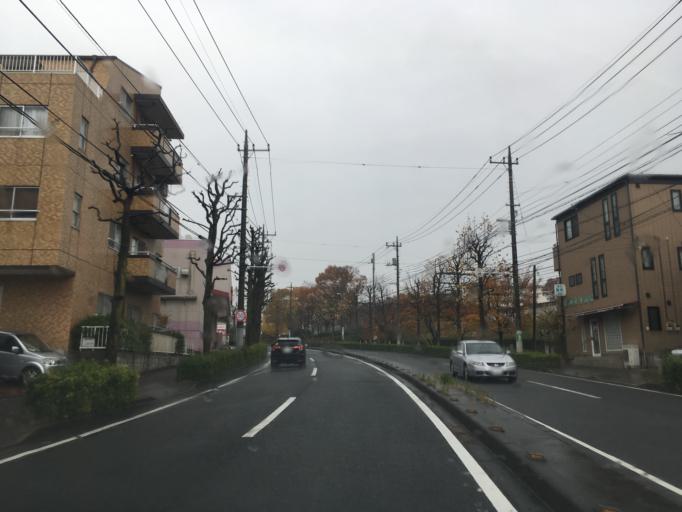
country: JP
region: Tokyo
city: Hino
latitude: 35.6276
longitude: 139.4559
